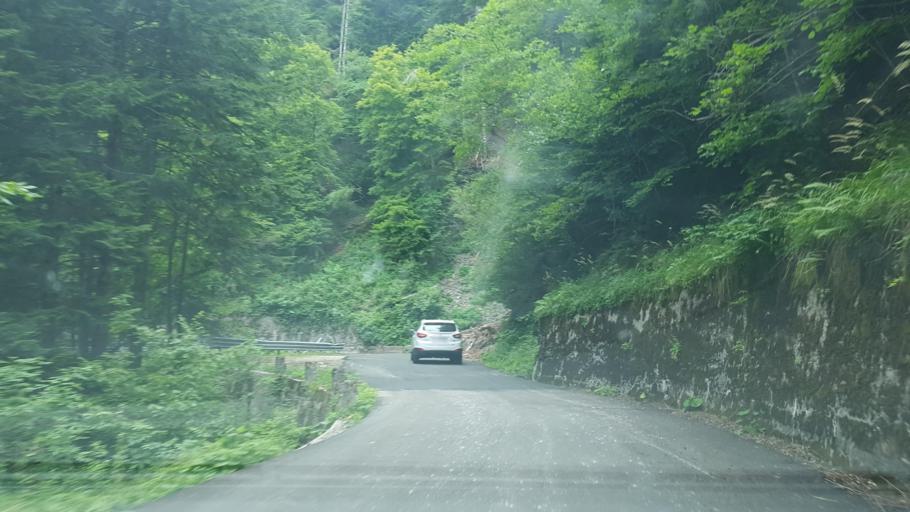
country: IT
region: Friuli Venezia Giulia
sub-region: Provincia di Udine
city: Paularo
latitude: 46.5569
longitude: 13.1277
